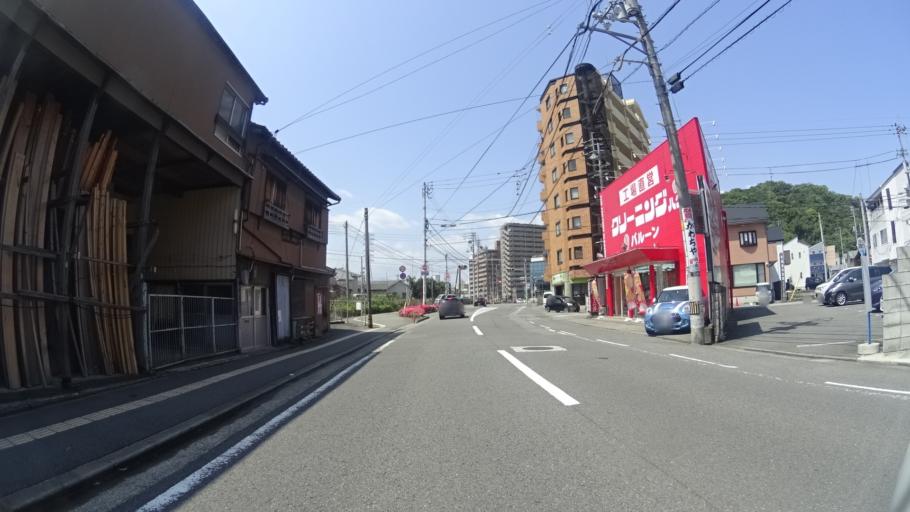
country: JP
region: Tokushima
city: Tokushima-shi
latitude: 34.0586
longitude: 134.5503
